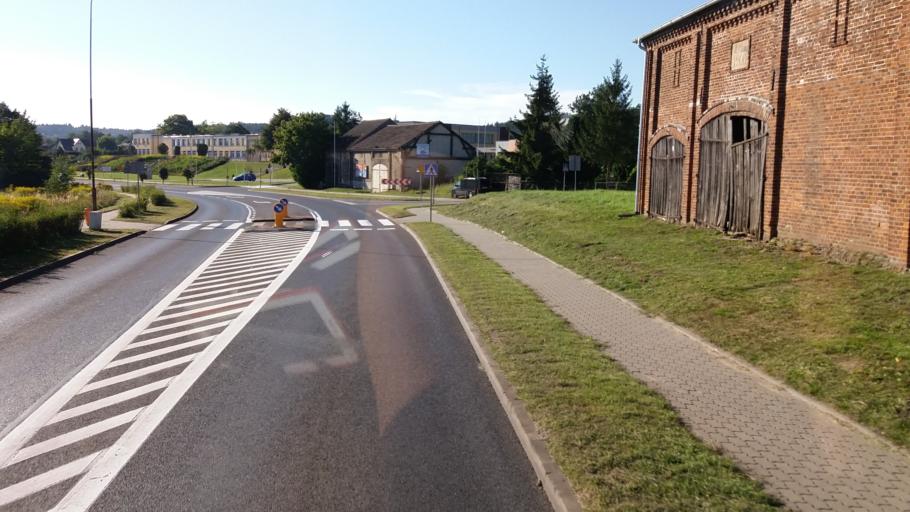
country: PL
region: West Pomeranian Voivodeship
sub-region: Powiat drawski
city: Kalisz Pomorski
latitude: 53.2998
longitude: 15.9172
